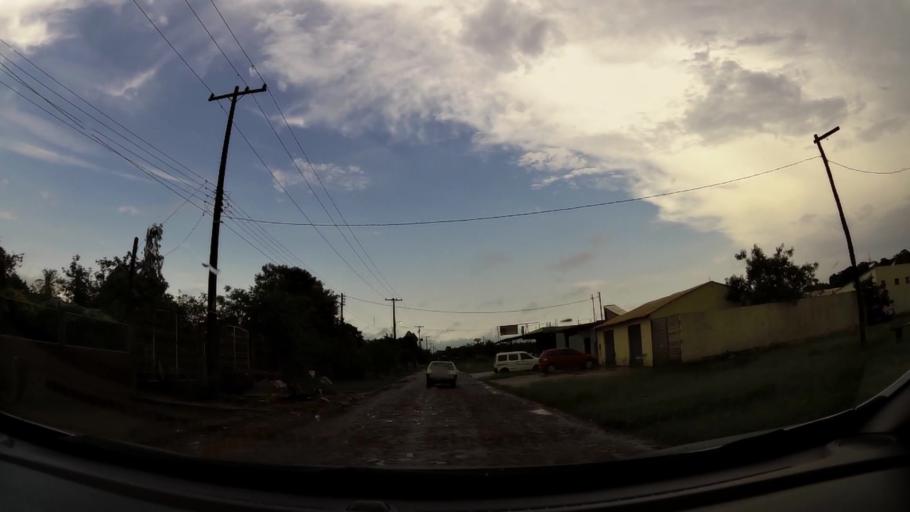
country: PY
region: Alto Parana
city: Presidente Franco
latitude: -25.5344
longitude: -54.6625
